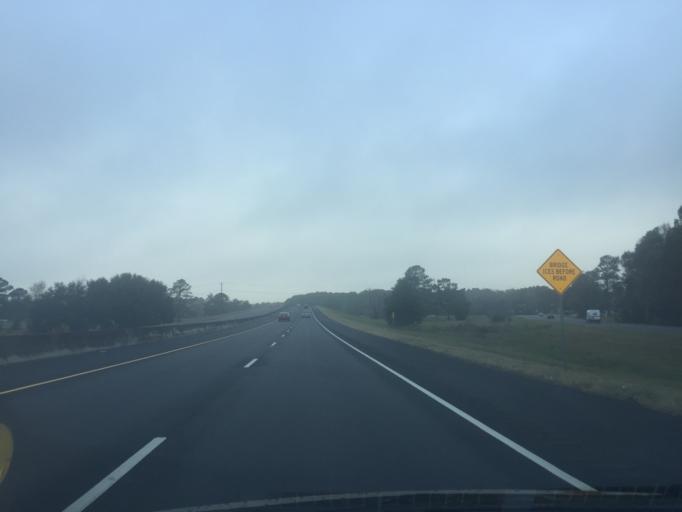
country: US
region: Georgia
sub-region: Chatham County
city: Georgetown
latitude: 31.9986
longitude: -81.2447
